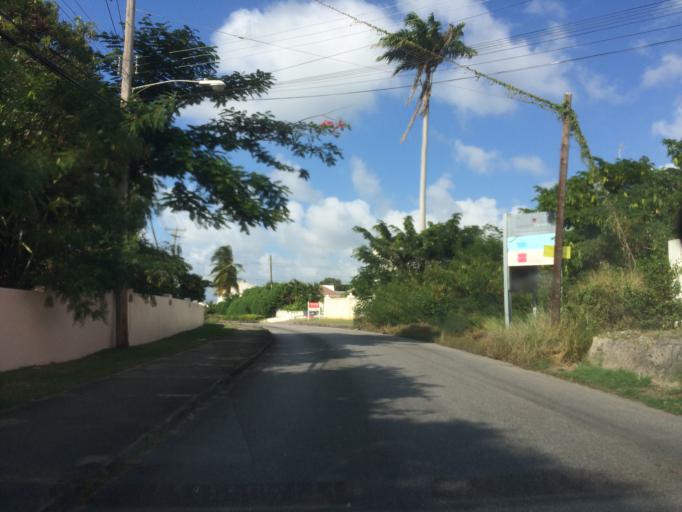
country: BB
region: Saint James
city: Holetown
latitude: 13.2027
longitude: -59.6395
